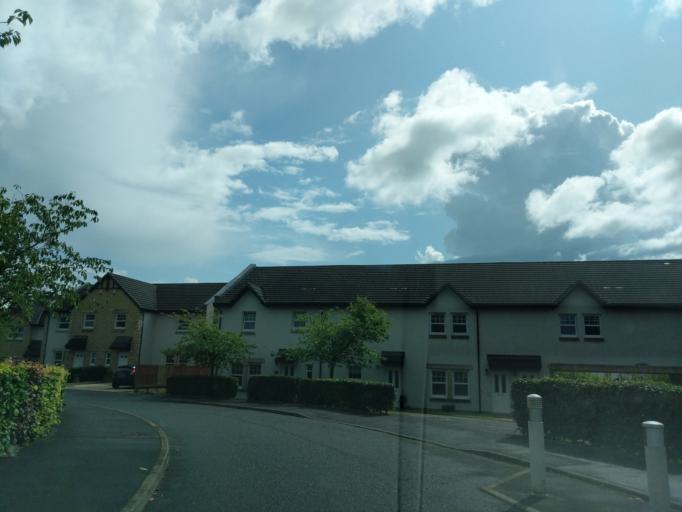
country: GB
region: Scotland
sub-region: East Ayrshire
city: Stewarton
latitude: 55.7118
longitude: -4.5318
